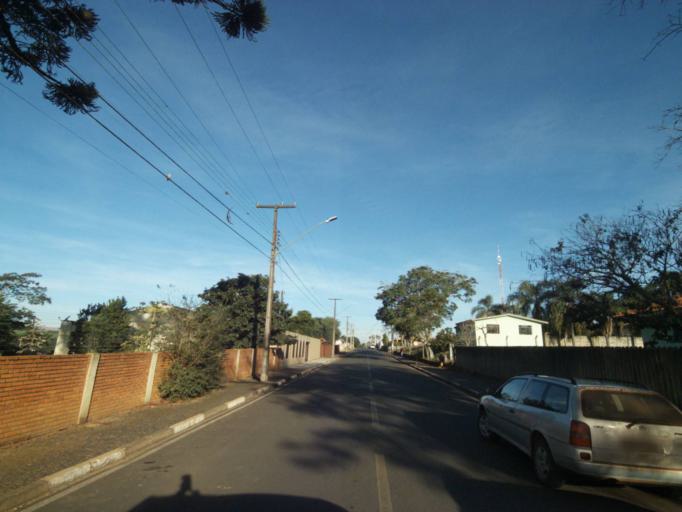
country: BR
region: Parana
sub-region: Tibagi
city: Tibagi
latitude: -24.5229
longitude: -50.4040
